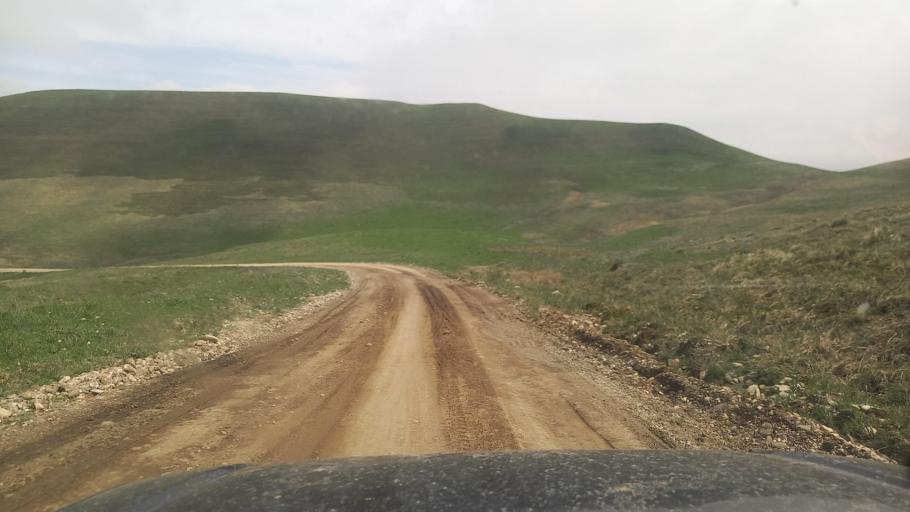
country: RU
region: Kabardino-Balkariya
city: Kamennomostskoye
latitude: 43.7800
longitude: 42.8646
